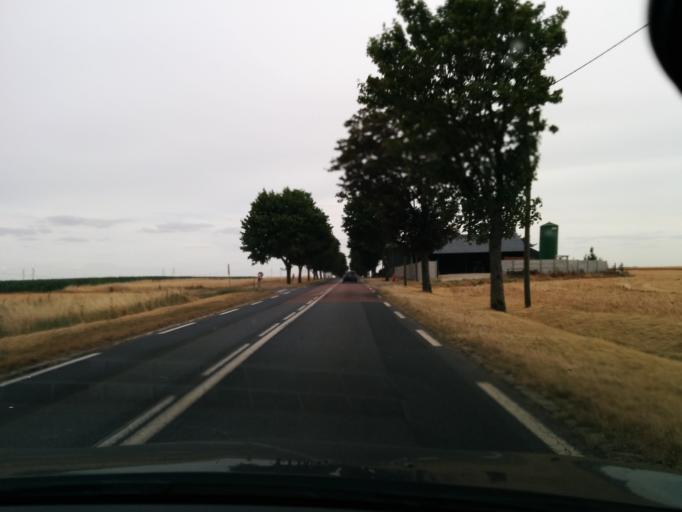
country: FR
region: Ile-de-France
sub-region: Departement de l'Essonne
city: Pussay
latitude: 48.3440
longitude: 1.9884
